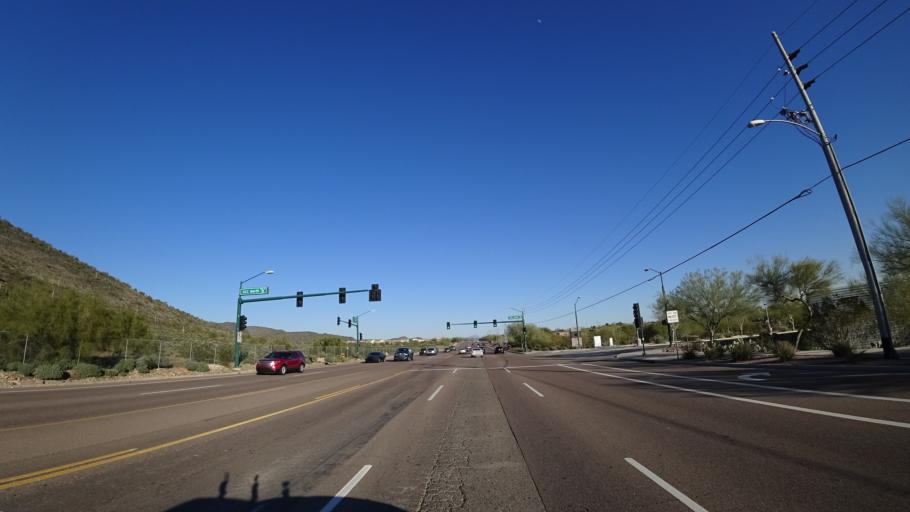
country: US
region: Arizona
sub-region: Maricopa County
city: Peoria
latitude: 33.7123
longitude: -112.1875
